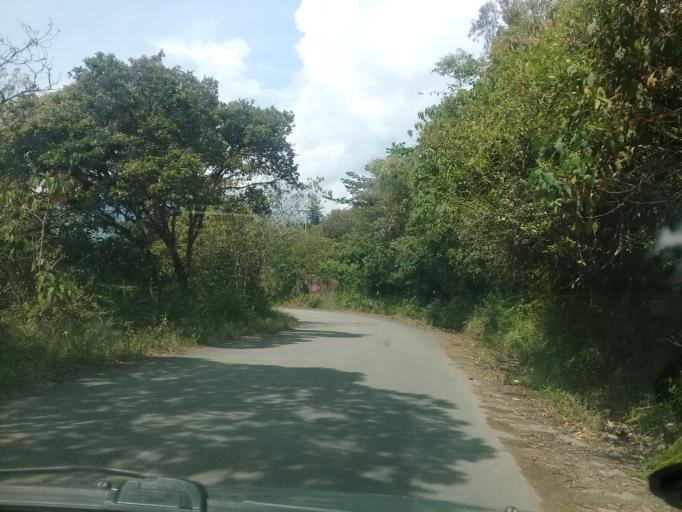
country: CO
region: Cundinamarca
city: Gachala
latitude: 4.6990
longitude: -73.4873
